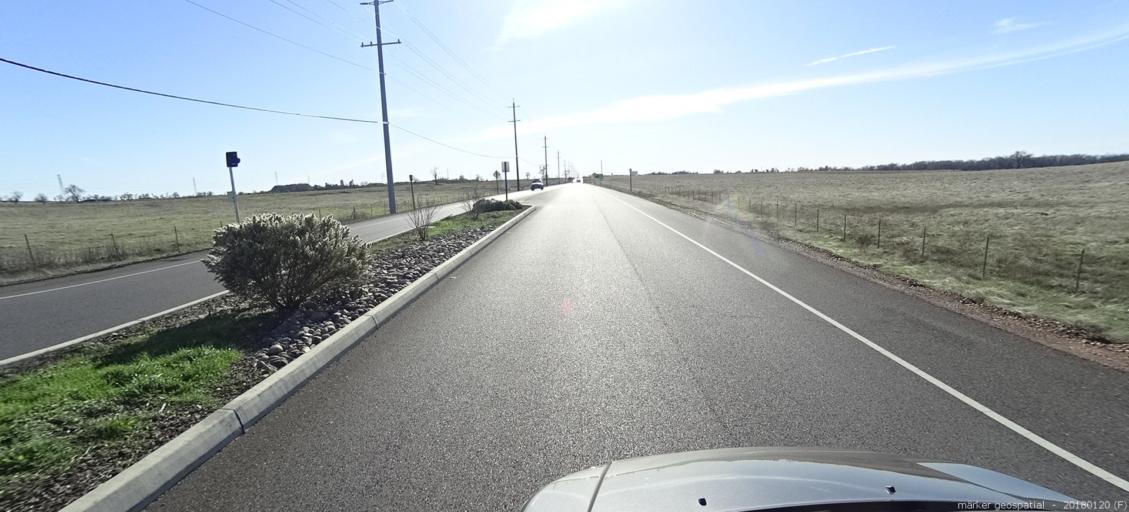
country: US
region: California
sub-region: Sacramento County
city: Gold River
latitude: 38.5935
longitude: -121.1786
